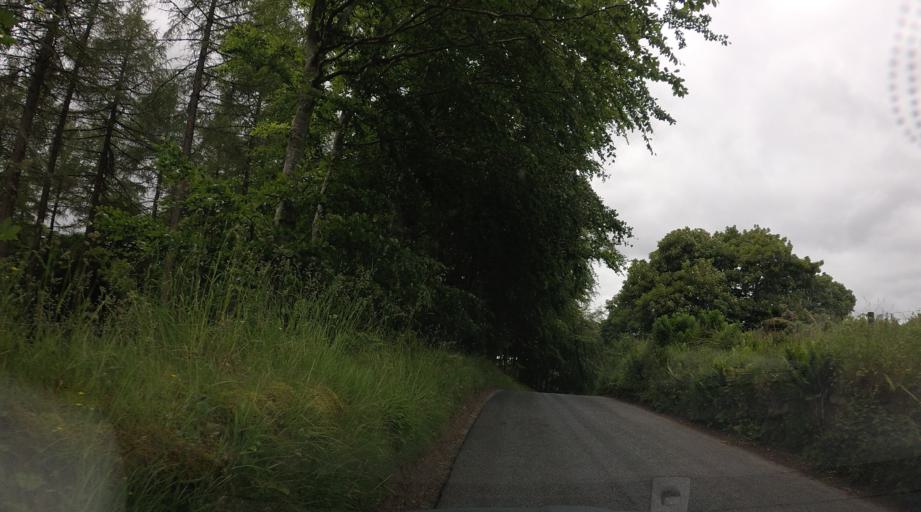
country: GB
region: Scotland
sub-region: Perth and Kinross
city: Aberfeldy
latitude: 56.7048
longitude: -4.1213
